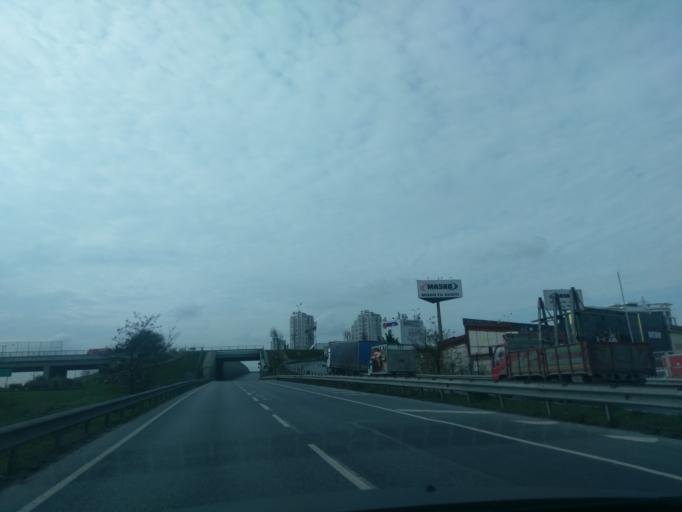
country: TR
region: Istanbul
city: Basaksehir
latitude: 41.0644
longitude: 28.7891
